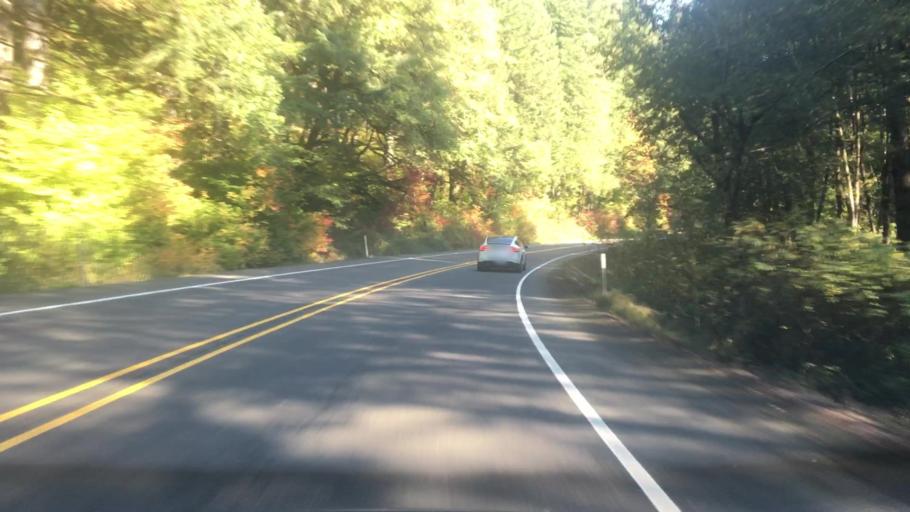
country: US
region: Oregon
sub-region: Lincoln County
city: Rose Lodge
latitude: 45.0559
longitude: -123.7647
